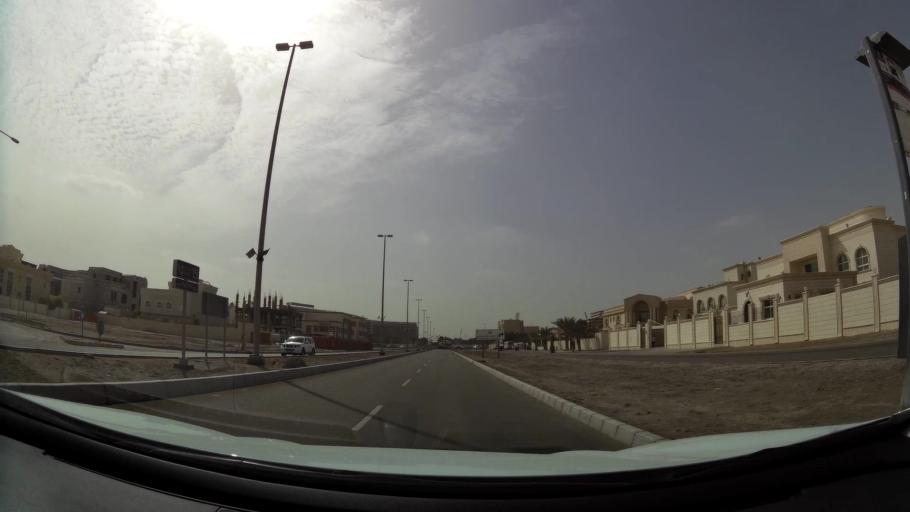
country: AE
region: Abu Dhabi
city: Abu Dhabi
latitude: 24.4097
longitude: 54.5532
